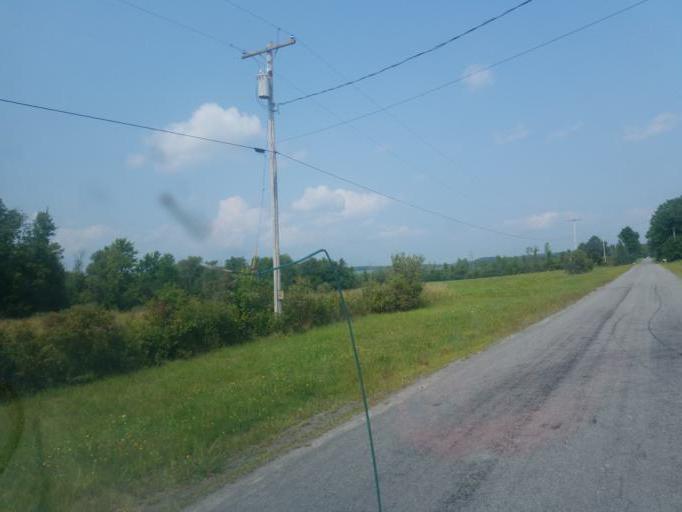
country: US
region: New York
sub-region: Montgomery County
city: Wellsville
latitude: 42.8521
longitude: -74.3430
